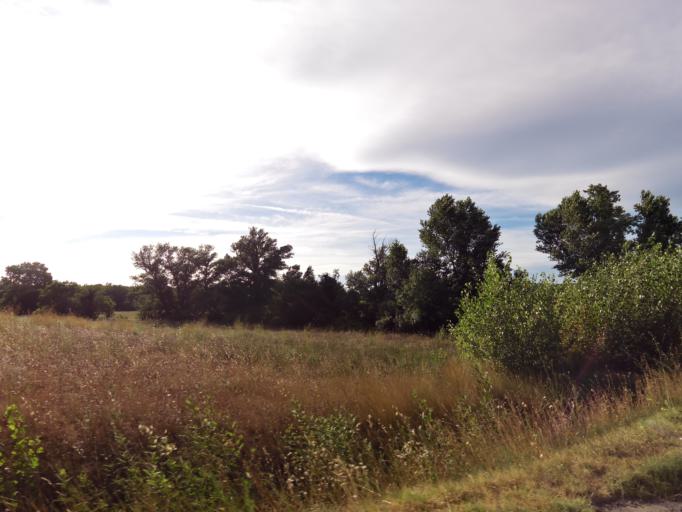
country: FR
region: Languedoc-Roussillon
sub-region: Departement du Gard
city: Villevieille
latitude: 43.8388
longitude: 4.1412
